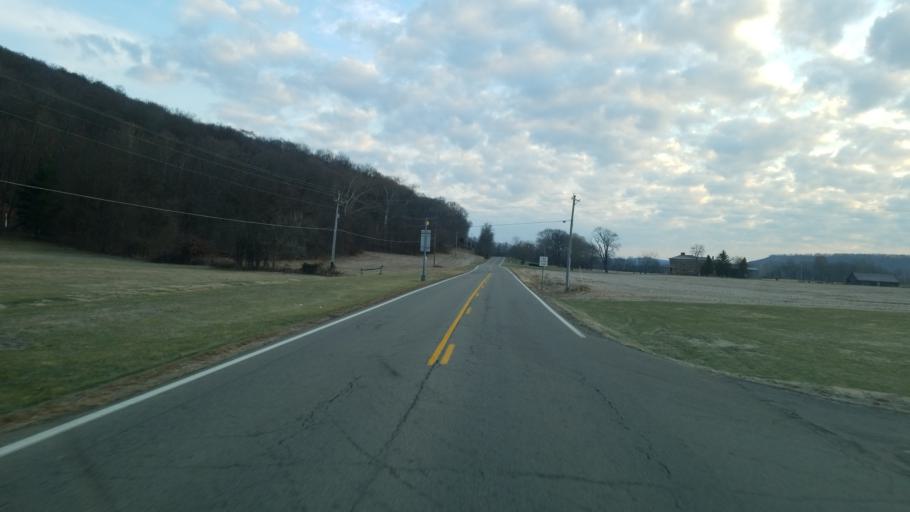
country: US
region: Ohio
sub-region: Ross County
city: Frankfort
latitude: 39.2445
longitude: -83.2145
